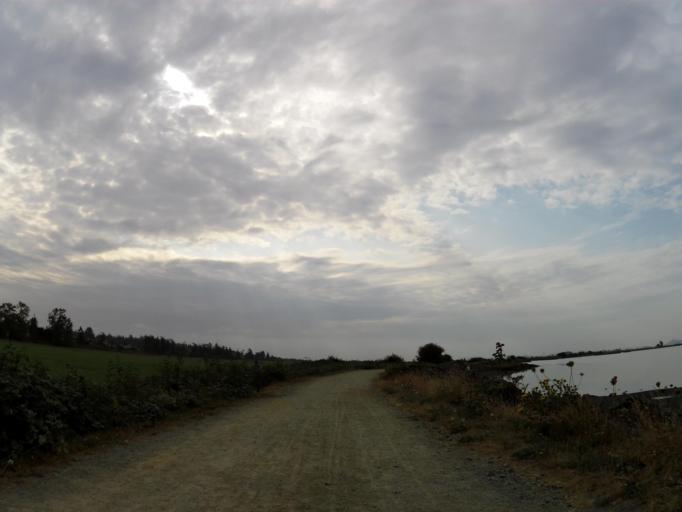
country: US
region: Washington
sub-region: Skagit County
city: Burlington
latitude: 48.4774
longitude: -122.4699
